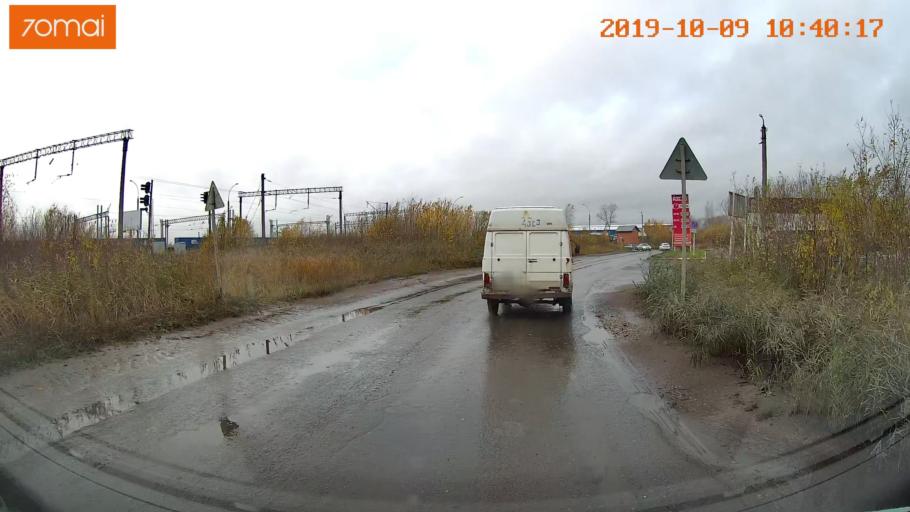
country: RU
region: Vologda
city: Vologda
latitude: 59.2335
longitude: 39.8379
